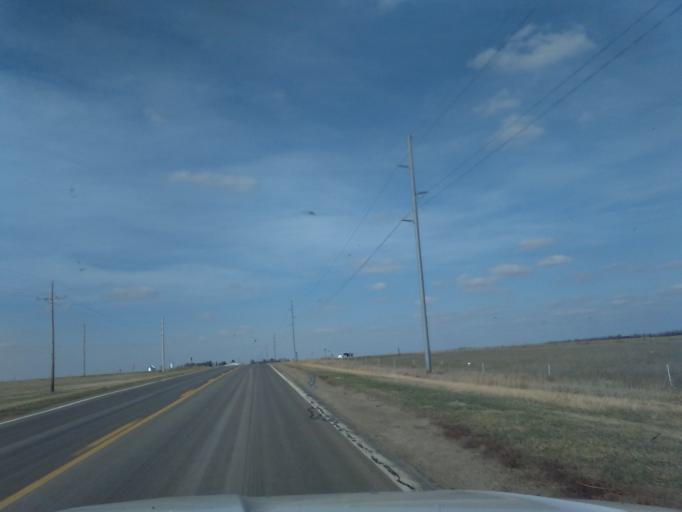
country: US
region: Nebraska
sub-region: Gage County
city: Beatrice
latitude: 40.1886
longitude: -96.9353
